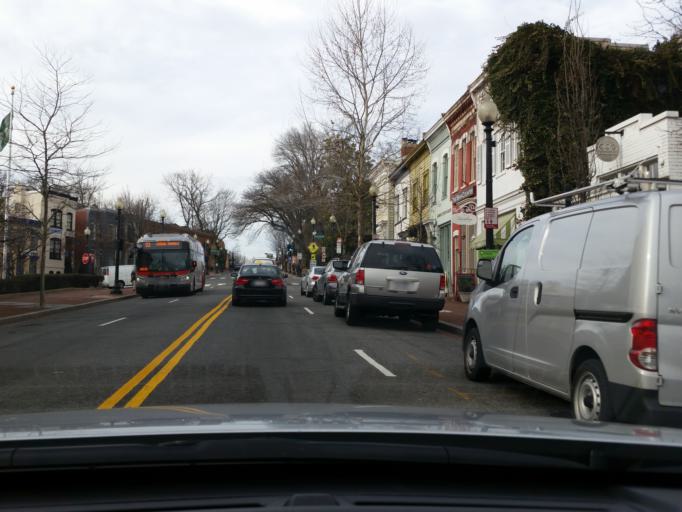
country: US
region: Washington, D.C.
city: Washington, D.C.
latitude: 38.9118
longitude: -77.0657
